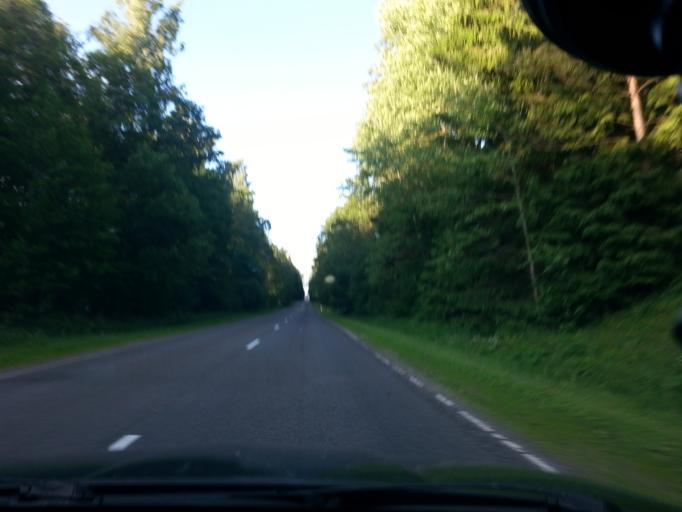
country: BY
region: Minsk
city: Svir
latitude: 54.9054
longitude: 26.4251
